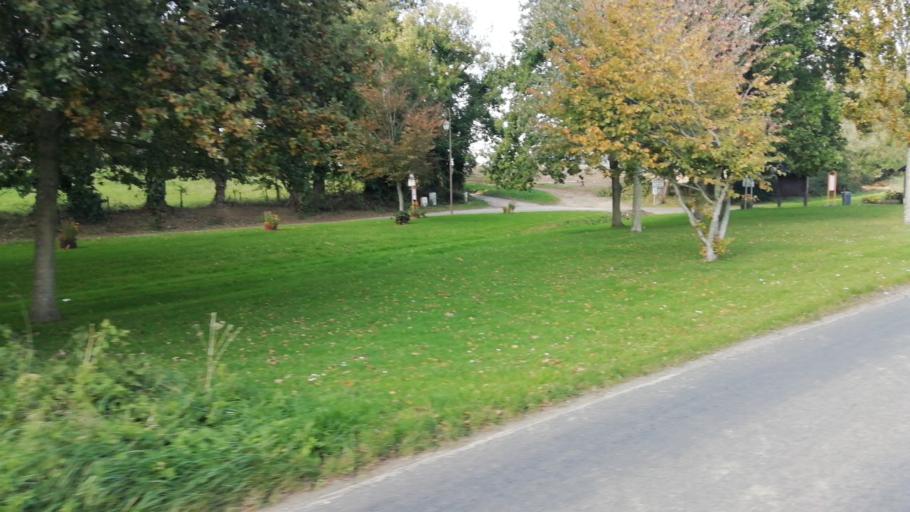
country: FR
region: Haute-Normandie
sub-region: Departement de la Seine-Maritime
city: Turretot
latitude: 49.6050
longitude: 0.2198
